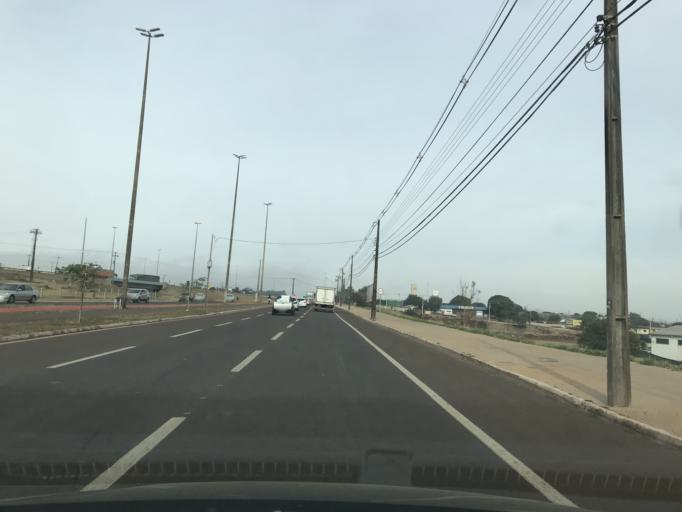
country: BR
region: Parana
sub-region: Cascavel
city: Cascavel
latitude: -24.9779
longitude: -53.4985
